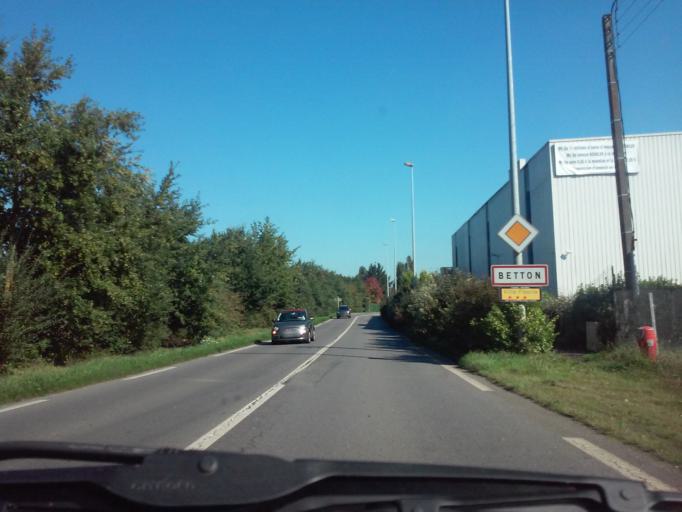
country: FR
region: Brittany
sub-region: Departement d'Ille-et-Vilaine
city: Betton
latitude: 48.1671
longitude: -1.6448
